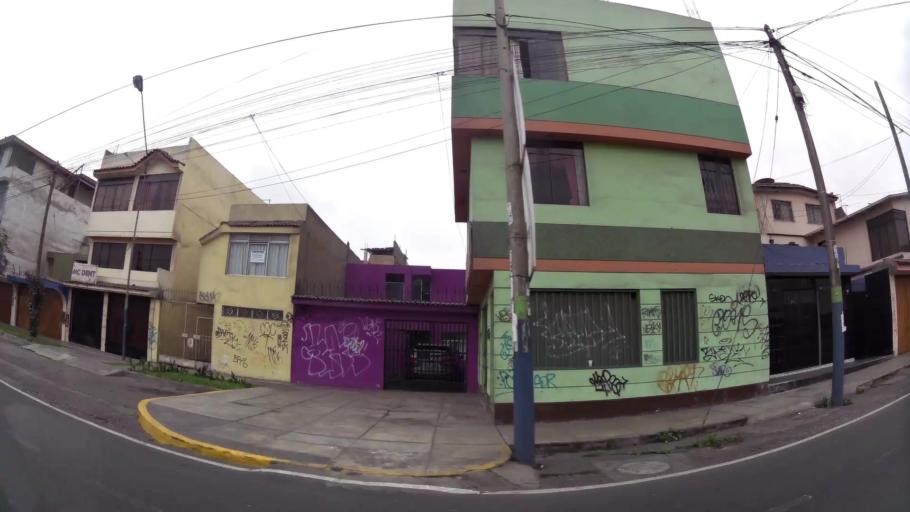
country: PE
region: Lima
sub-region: Lima
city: San Luis
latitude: -12.0802
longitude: -77.0027
